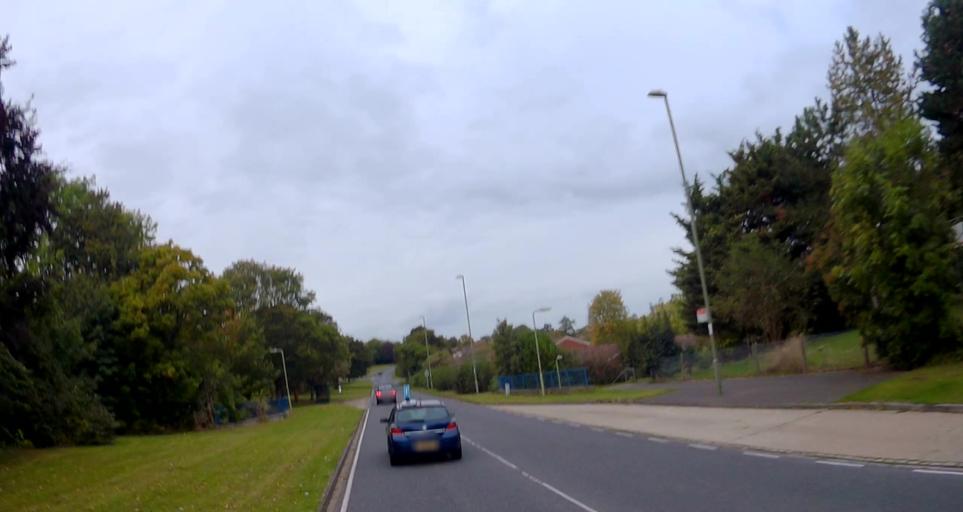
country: GB
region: England
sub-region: Hampshire
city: Basingstoke
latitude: 51.2404
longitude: -1.1140
